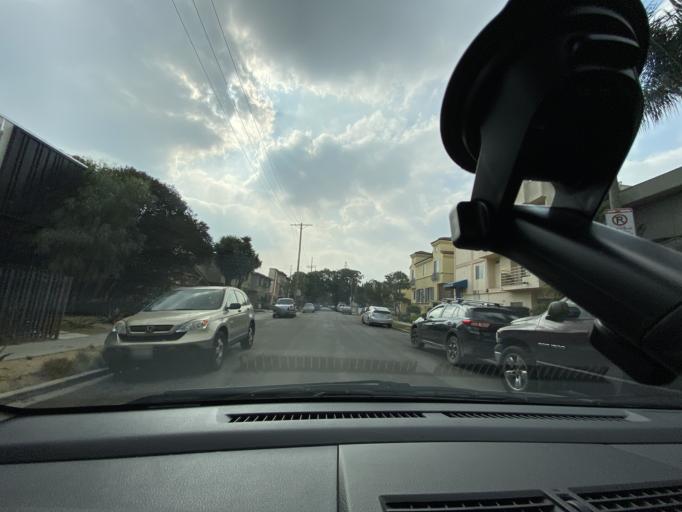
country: US
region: California
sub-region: Los Angeles County
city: Culver City
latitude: 34.0326
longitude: -118.3929
